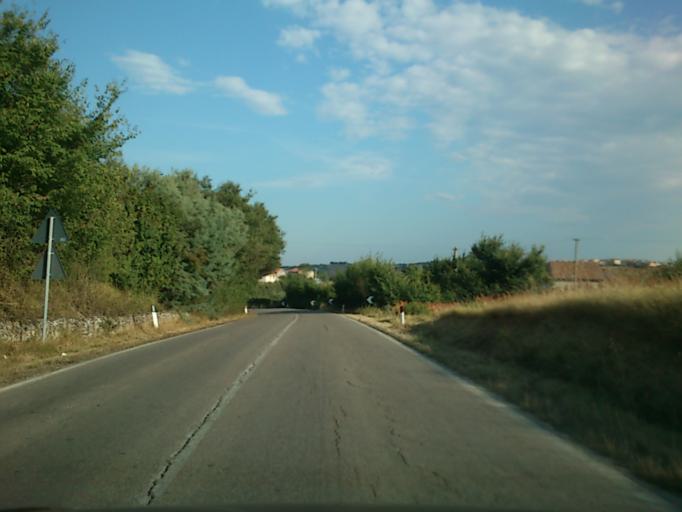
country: IT
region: The Marches
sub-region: Provincia di Pesaro e Urbino
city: San Costanzo
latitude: 43.7809
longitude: 13.0714
